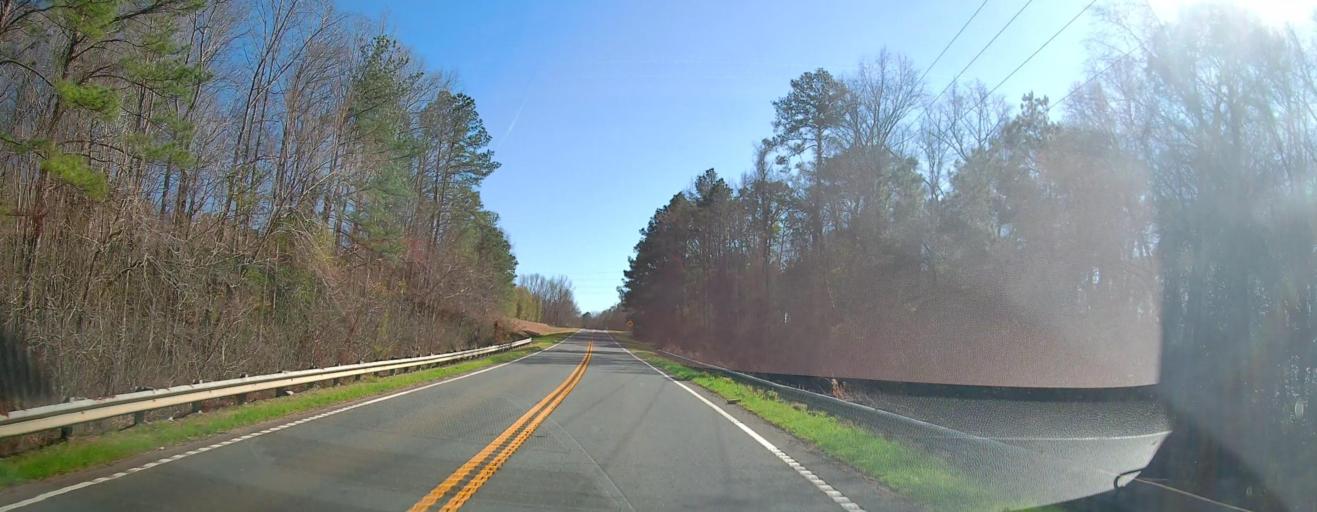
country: US
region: Georgia
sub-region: Macon County
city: Oglethorpe
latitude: 32.2938
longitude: -84.0763
